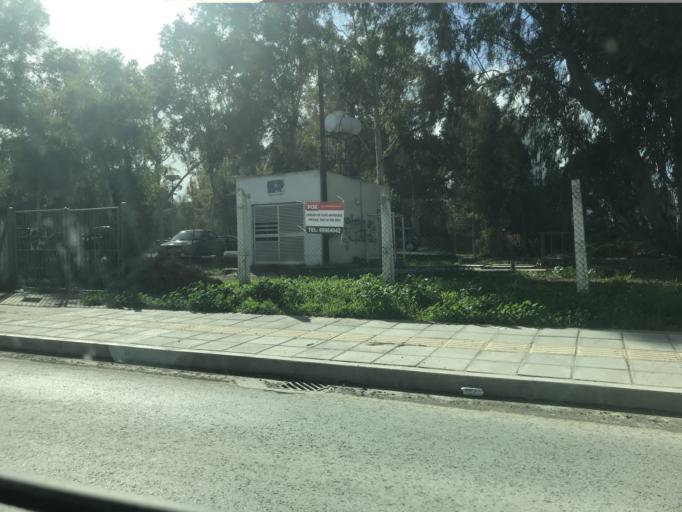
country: CY
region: Lefkosia
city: Nicosia
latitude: 35.1645
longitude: 33.3831
